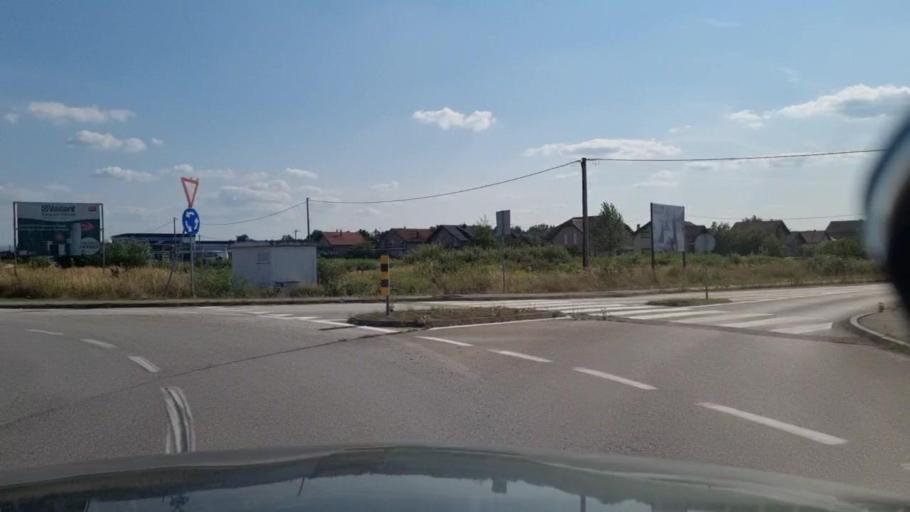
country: BA
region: Federation of Bosnia and Herzegovina
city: Odzak
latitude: 45.0306
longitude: 18.3265
